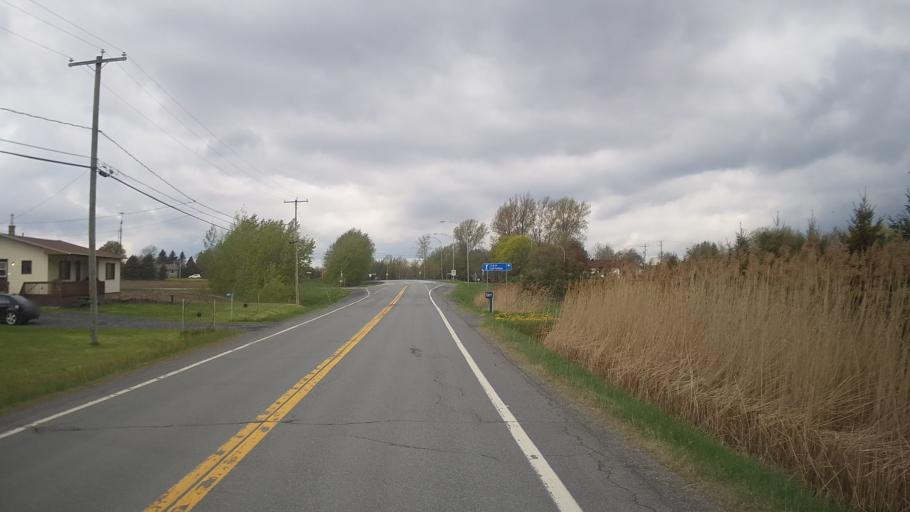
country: CA
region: Quebec
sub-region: Monteregie
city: Farnham
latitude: 45.2694
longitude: -72.9469
